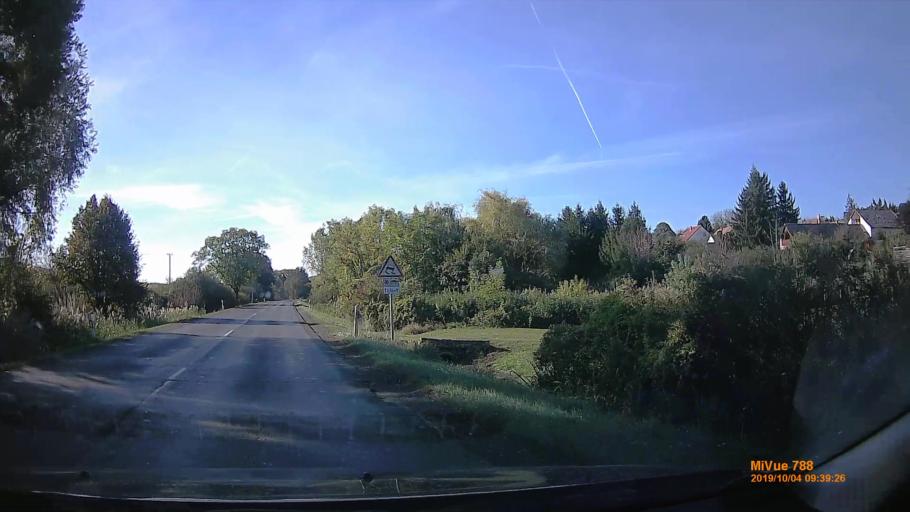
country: HU
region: Somogy
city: Kaposvar
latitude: 46.4504
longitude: 17.8046
